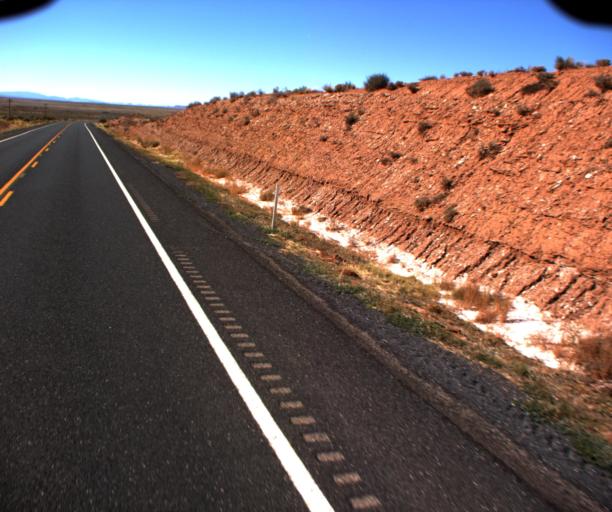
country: US
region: Arizona
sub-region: Coconino County
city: Fredonia
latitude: 36.9036
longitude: -112.5958
